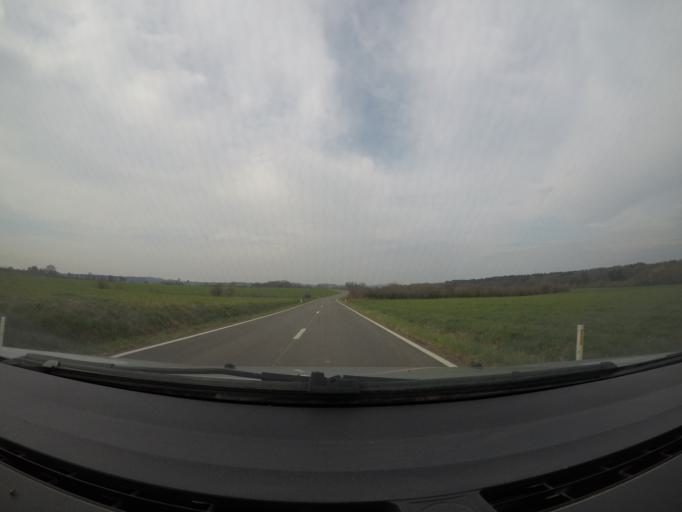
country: BE
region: Wallonia
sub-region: Province du Luxembourg
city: Tintigny
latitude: 49.7164
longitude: 5.4635
